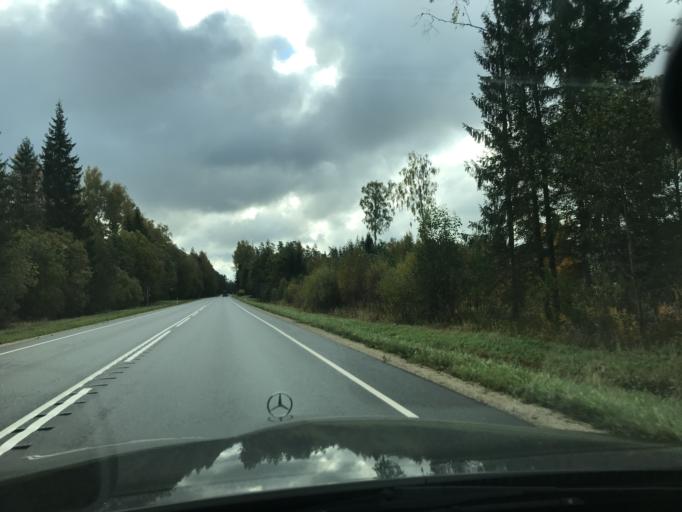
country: EE
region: Viljandimaa
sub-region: Karksi vald
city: Karksi-Nuia
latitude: 58.0334
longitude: 25.6473
